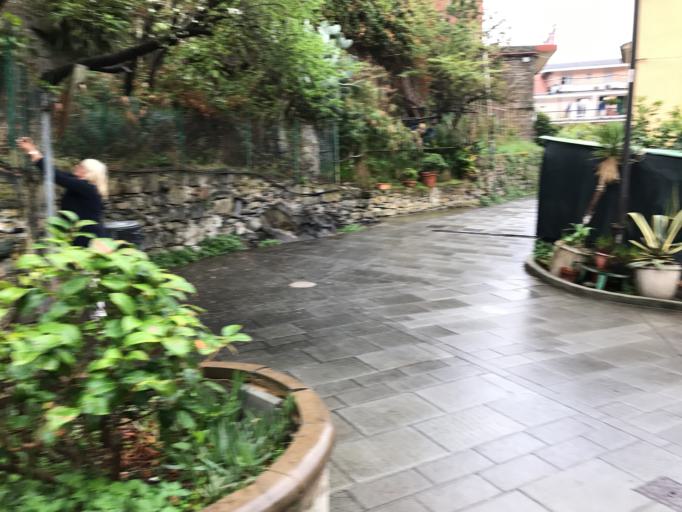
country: IT
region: Liguria
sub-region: Provincia di La Spezia
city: Riomaggiore
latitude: 44.1021
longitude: 9.7364
